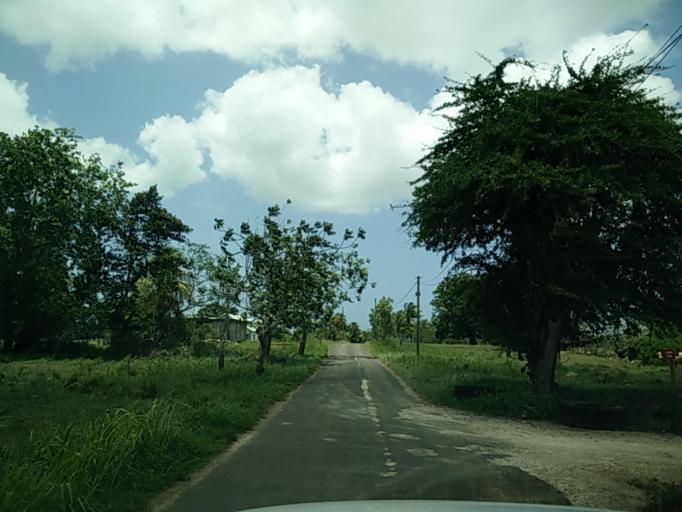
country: GP
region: Guadeloupe
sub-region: Guadeloupe
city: Les Abymes
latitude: 16.2863
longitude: -61.5229
